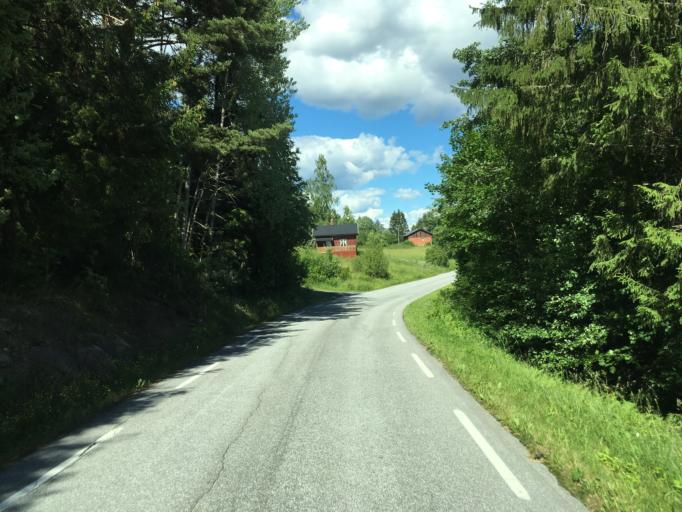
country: NO
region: Oppland
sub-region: Jevnaker
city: Jevnaker
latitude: 60.3436
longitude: 10.3593
